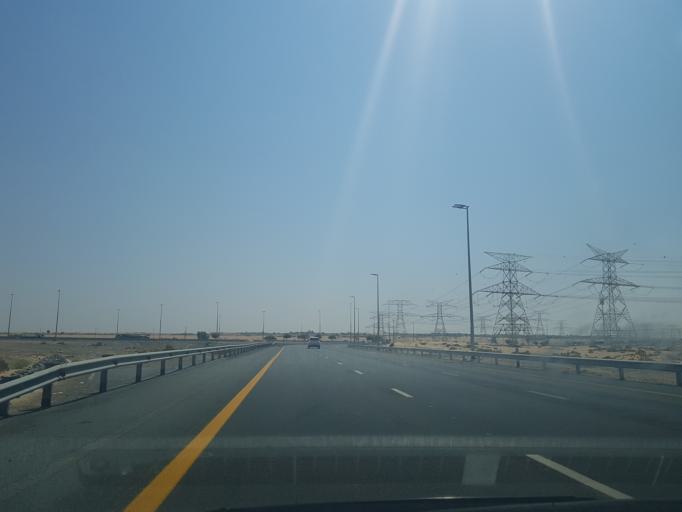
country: AE
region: Ash Shariqah
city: Sharjah
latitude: 25.2375
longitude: 55.5633
